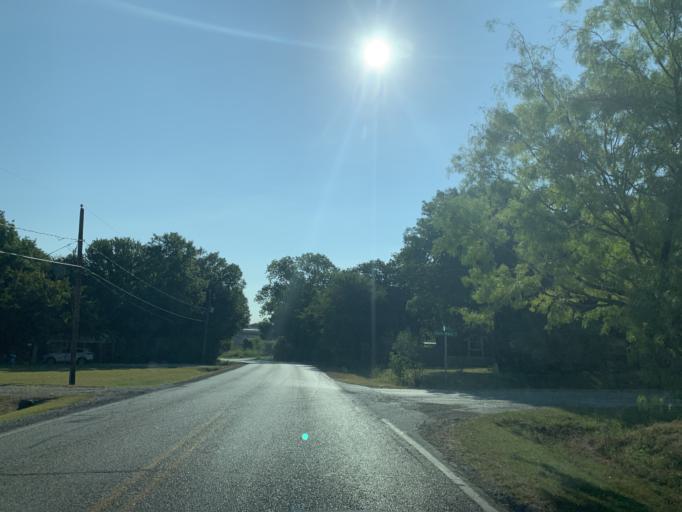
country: US
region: Texas
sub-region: Tarrant County
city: Lakeside
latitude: 32.8548
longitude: -97.5153
